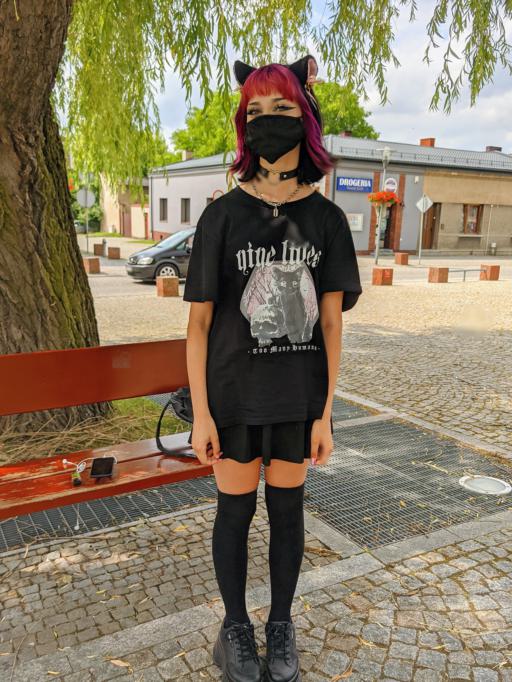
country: PL
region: Silesian Voivodeship
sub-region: Powiat klobucki
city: Klobuck
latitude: 50.9046
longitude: 18.9367
